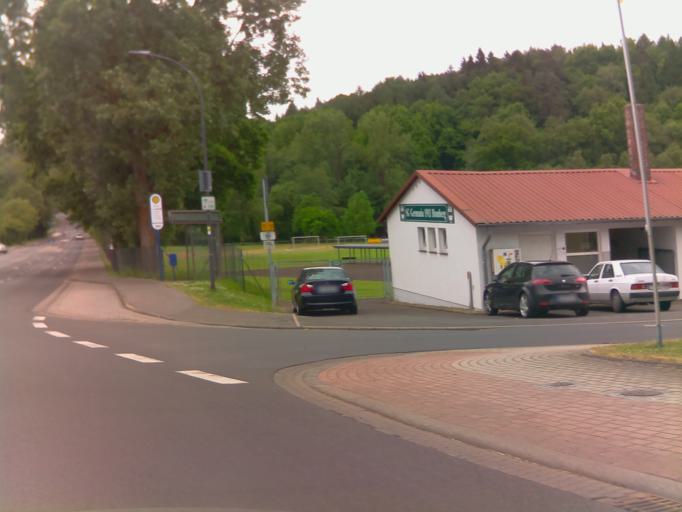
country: DE
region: Hesse
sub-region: Regierungsbezirk Giessen
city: Homberg
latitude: 50.7250
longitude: 9.0020
